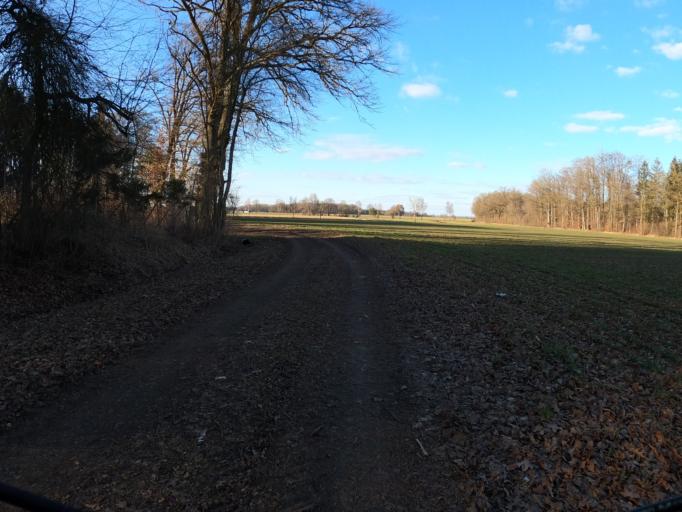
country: DE
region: Bavaria
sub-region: Swabia
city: Leipheim
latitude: 48.4183
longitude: 10.2031
